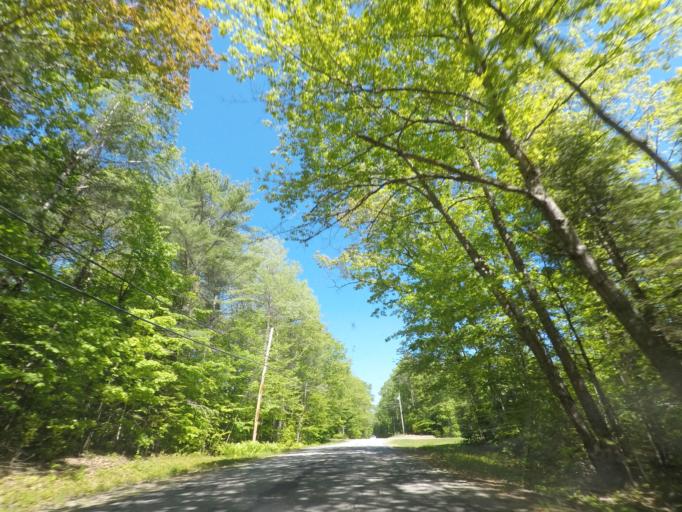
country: US
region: Maine
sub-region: Kennebec County
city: Manchester
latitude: 44.2542
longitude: -69.9015
